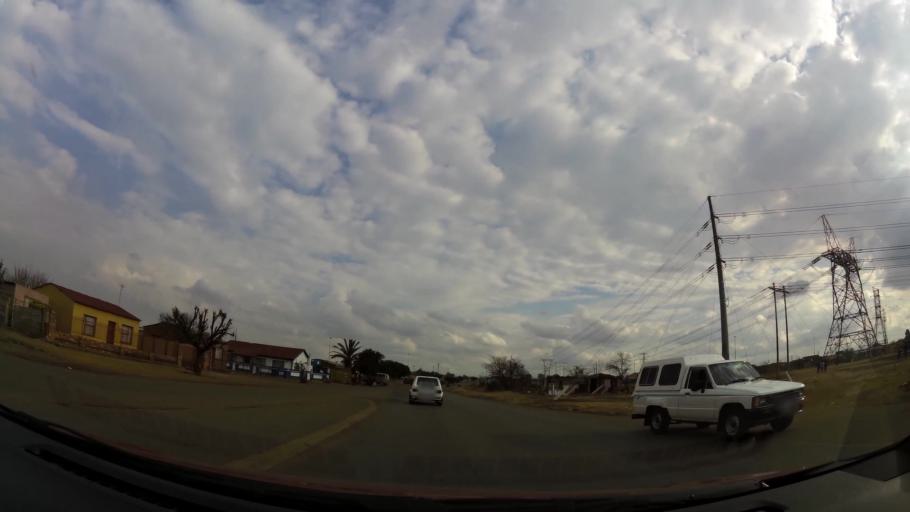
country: ZA
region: Gauteng
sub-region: Sedibeng District Municipality
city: Vereeniging
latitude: -26.6741
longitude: 27.8787
